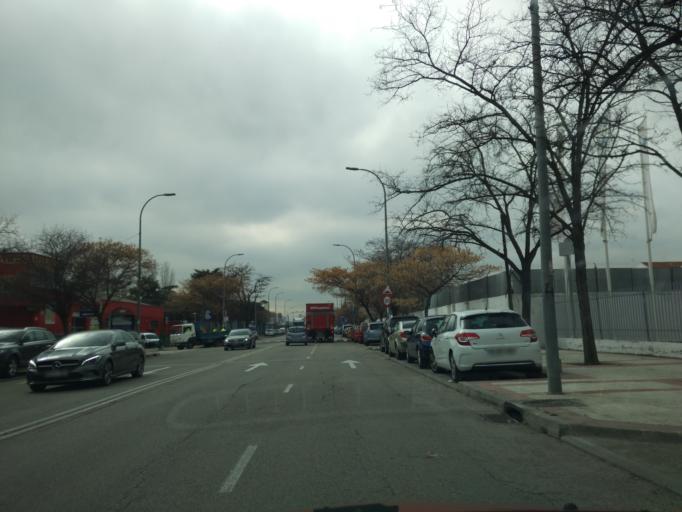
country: ES
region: Madrid
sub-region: Provincia de Madrid
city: Torrejon de Ardoz
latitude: 40.4550
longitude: -3.4876
